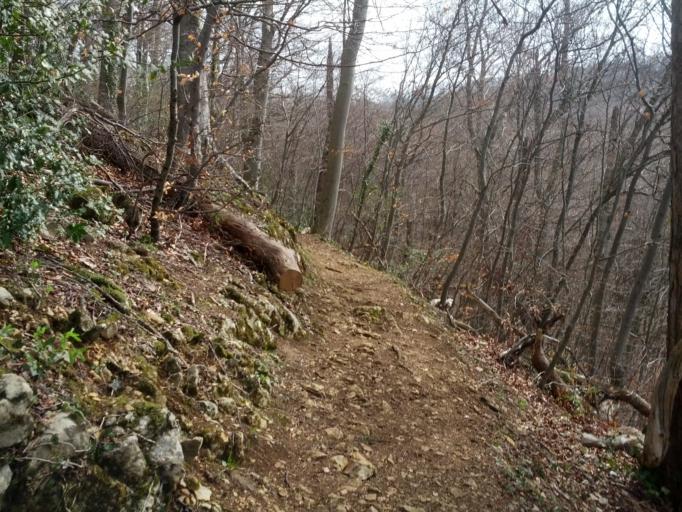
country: DE
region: Baden-Wuerttemberg
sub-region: Freiburg Region
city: Ebringen
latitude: 47.9587
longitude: 7.7957
